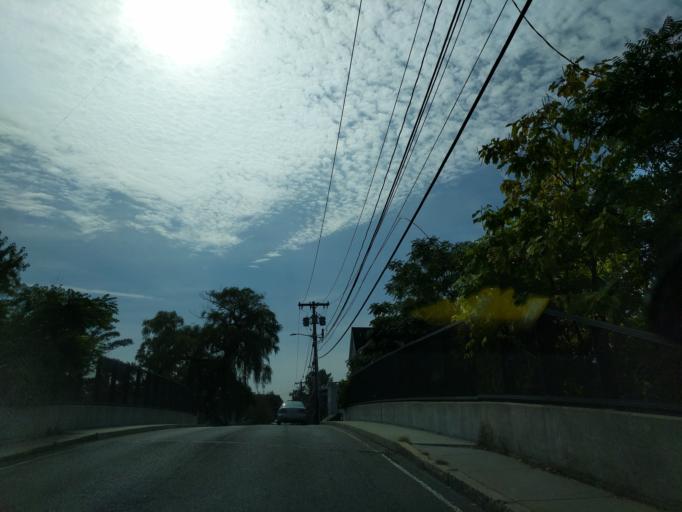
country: US
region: Massachusetts
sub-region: Middlesex County
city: Somerville
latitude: 42.3974
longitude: -71.1088
